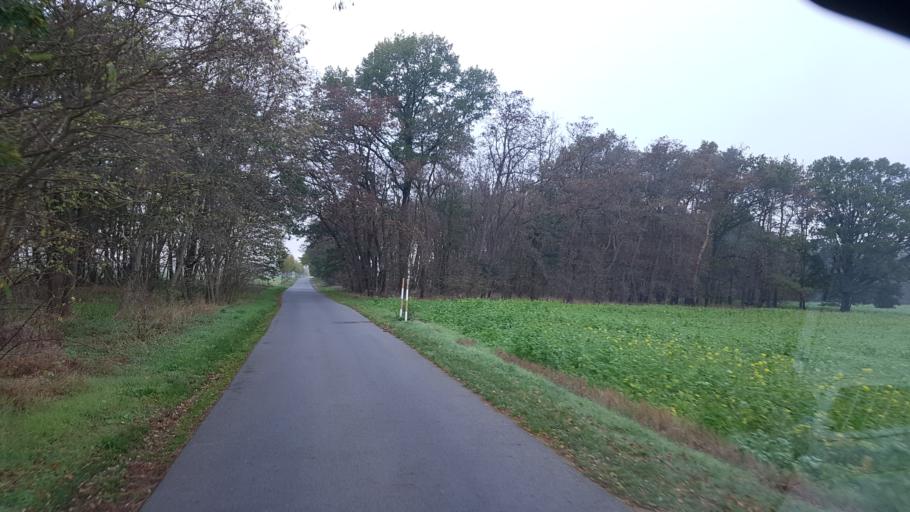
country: DE
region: Brandenburg
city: Schonewalde
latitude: 51.6750
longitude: 13.6278
